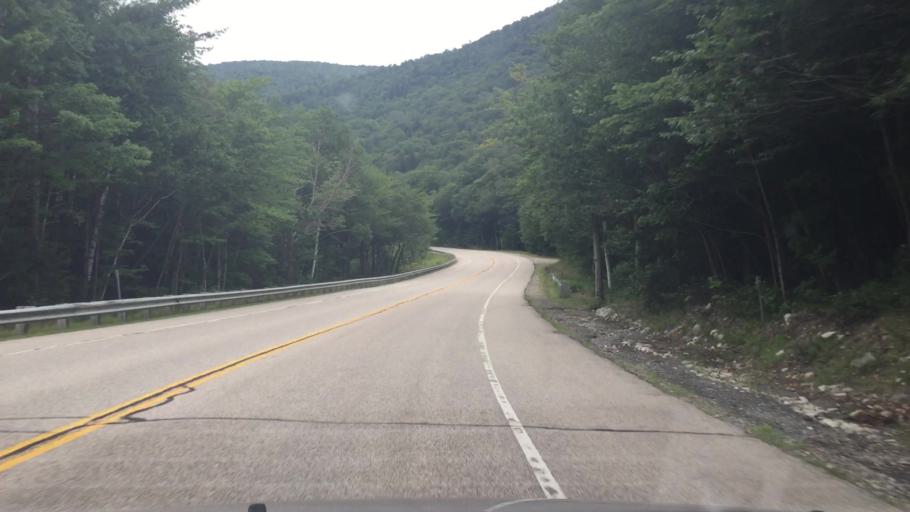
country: US
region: New Hampshire
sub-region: Grafton County
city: Deerfield
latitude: 44.1758
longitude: -71.3940
